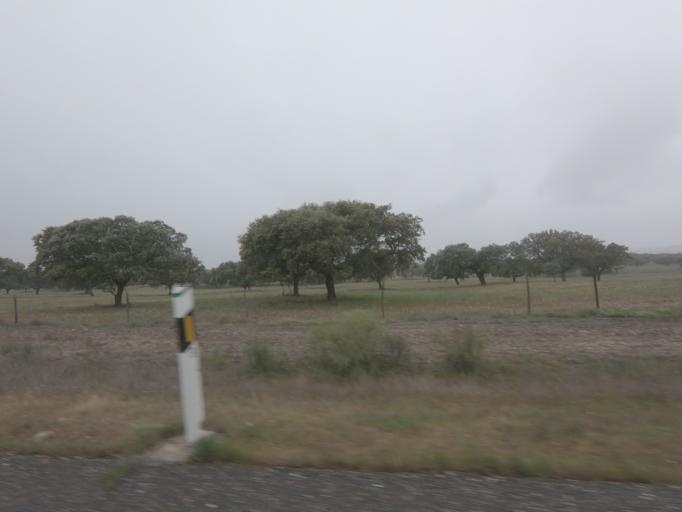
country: ES
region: Extremadura
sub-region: Provincia de Badajoz
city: La Roca de la Sierra
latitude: 39.0972
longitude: -6.7131
